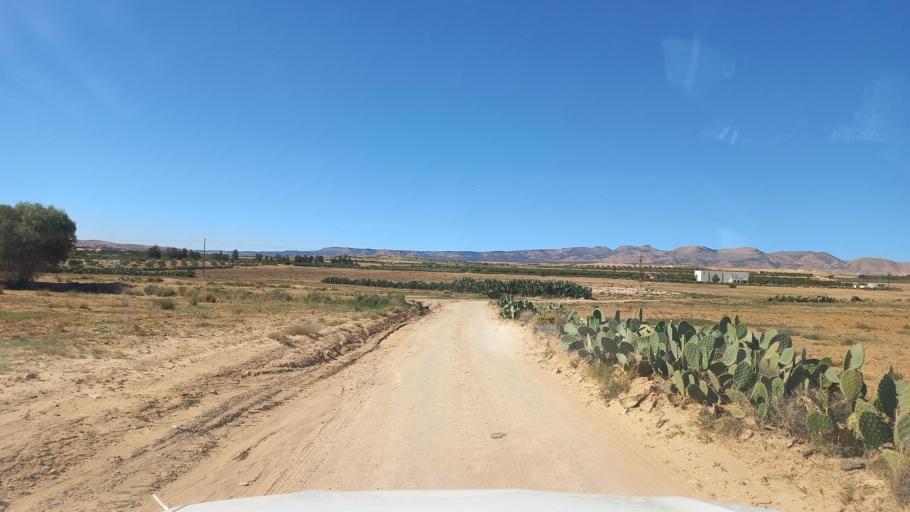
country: TN
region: Al Qasrayn
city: Sbiba
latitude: 35.3674
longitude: 9.0961
